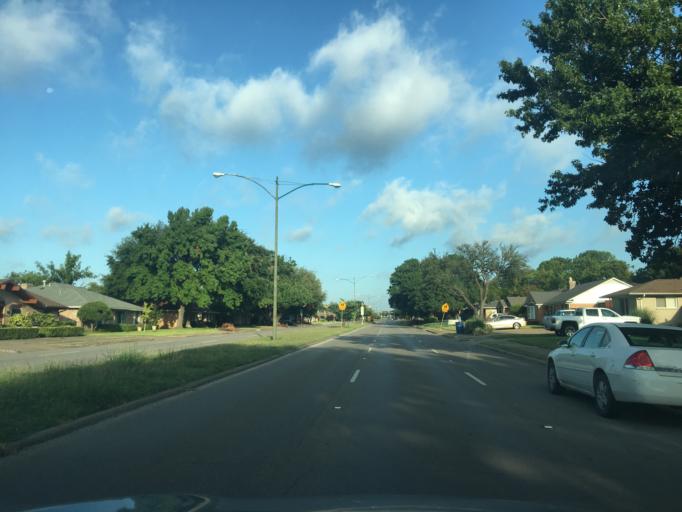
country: US
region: Texas
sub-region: Dallas County
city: Highland Park
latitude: 32.8510
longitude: -96.7547
